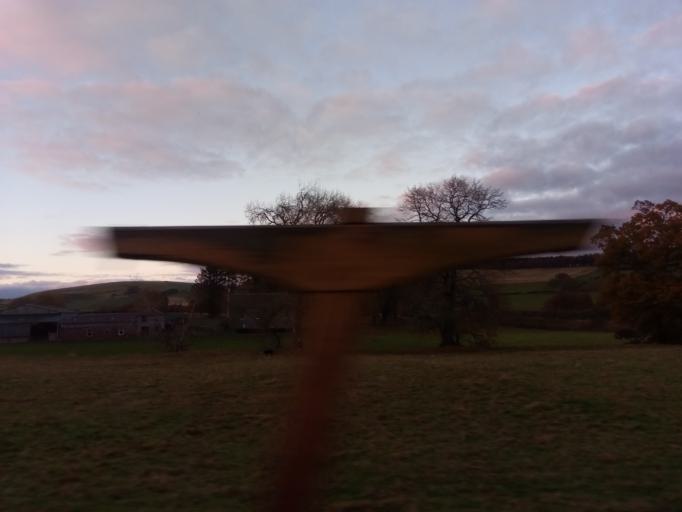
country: GB
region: Scotland
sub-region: The Scottish Borders
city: Lauder
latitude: 55.7724
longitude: -2.8021
